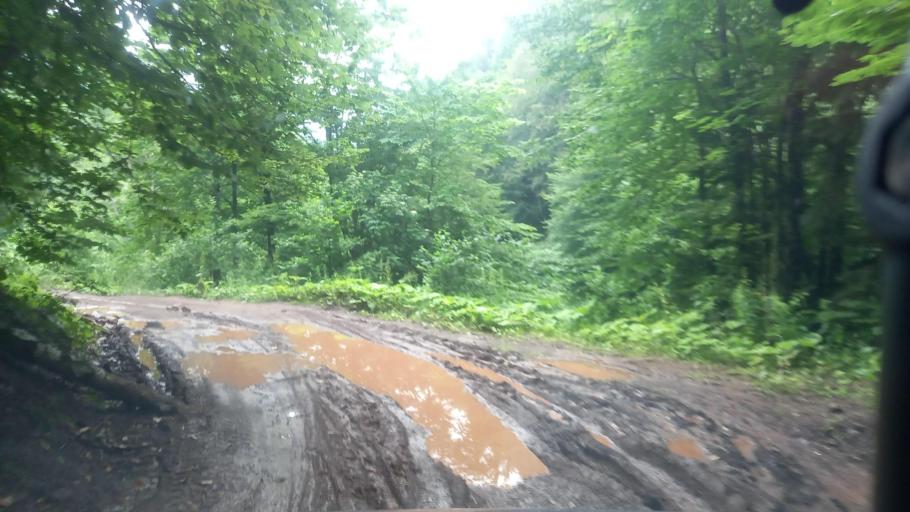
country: RU
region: Karachayevo-Cherkesiya
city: Kurdzhinovo
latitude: 43.8115
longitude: 40.8737
